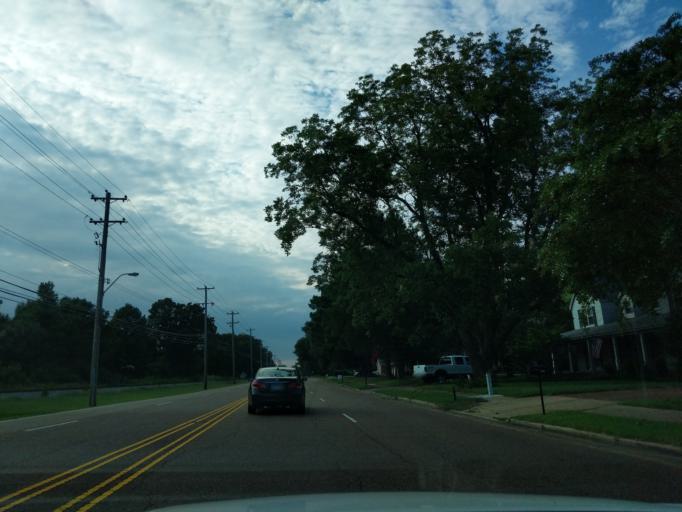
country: US
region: Tennessee
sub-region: Shelby County
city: Germantown
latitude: 35.0753
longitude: -89.7955
